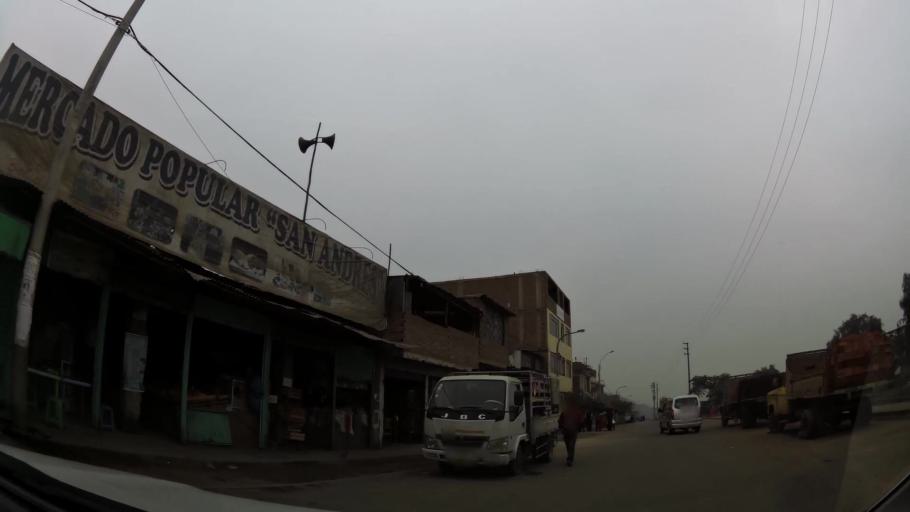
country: PE
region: Lima
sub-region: Lima
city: Urb. Santo Domingo
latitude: -11.9357
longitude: -76.9679
